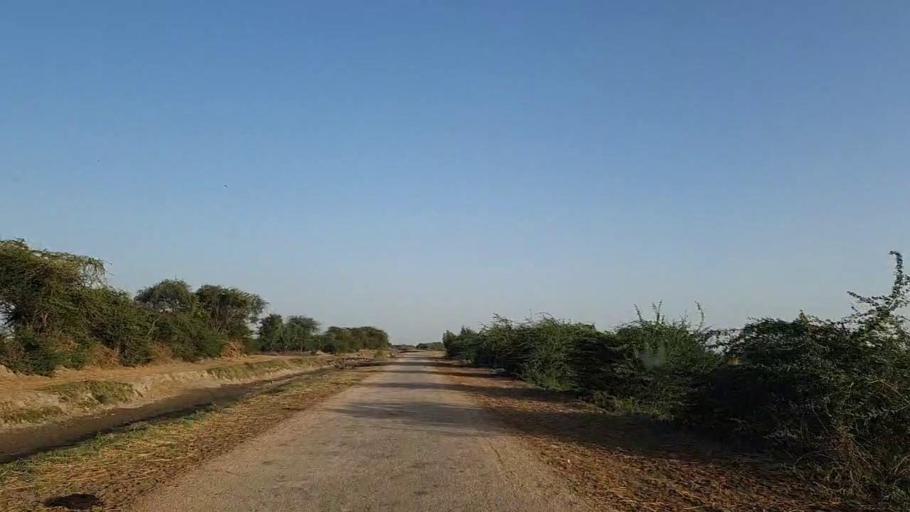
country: PK
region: Sindh
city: Jati
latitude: 24.4081
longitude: 68.3514
